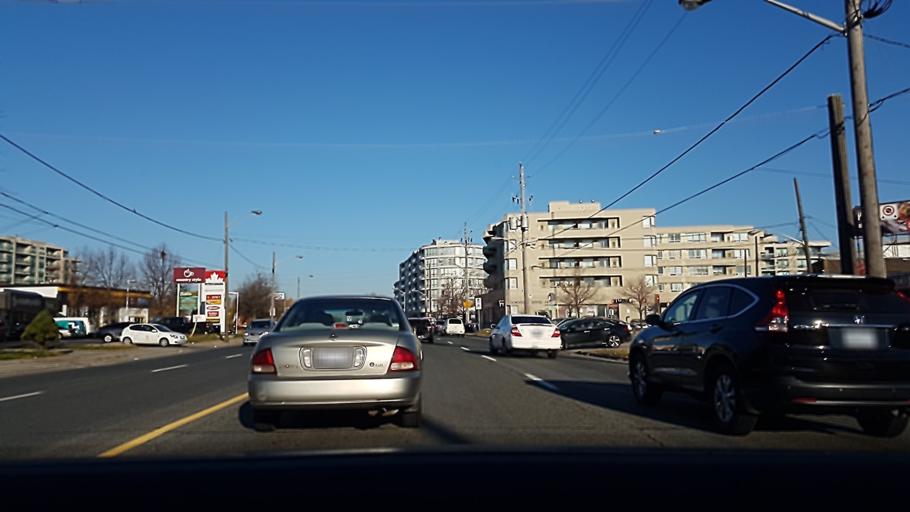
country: CA
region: Ontario
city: North York
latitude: 43.7504
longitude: -79.4557
